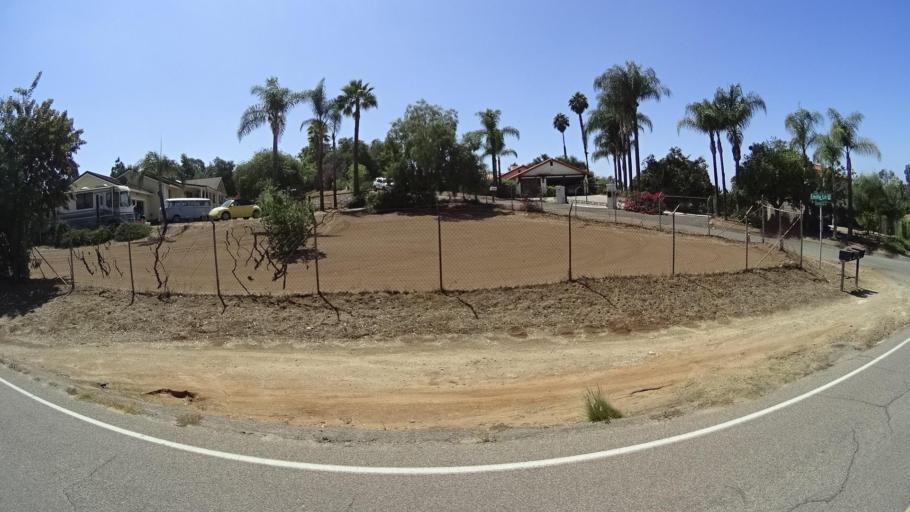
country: US
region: California
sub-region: San Diego County
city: Fallbrook
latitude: 33.3810
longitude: -117.2145
